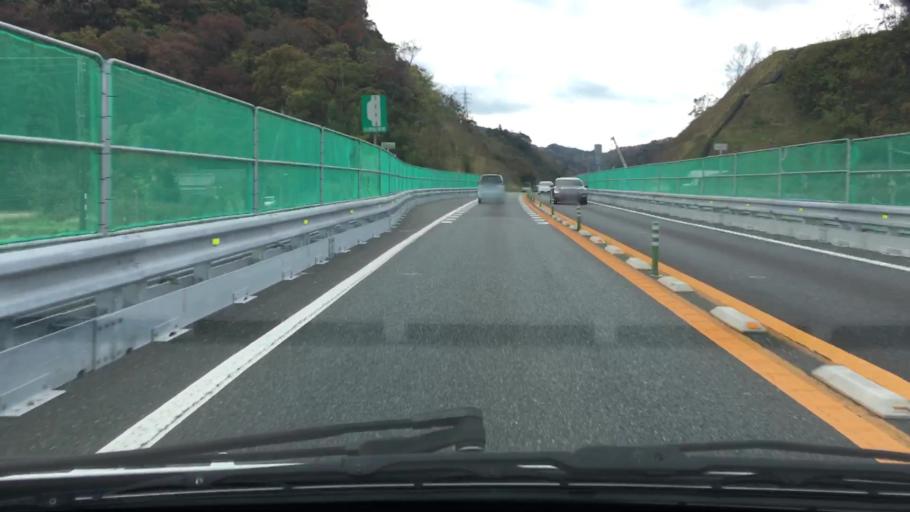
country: JP
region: Chiba
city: Kimitsu
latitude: 35.2121
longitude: 139.8845
